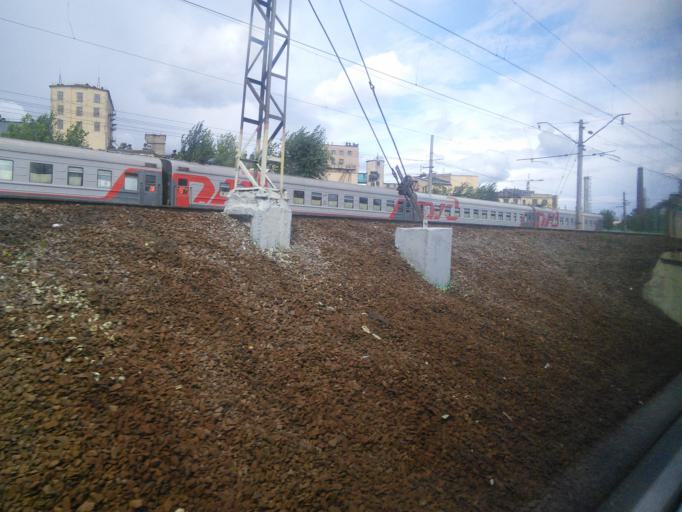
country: RU
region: Moscow
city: Lefortovo
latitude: 55.7820
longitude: 37.6831
